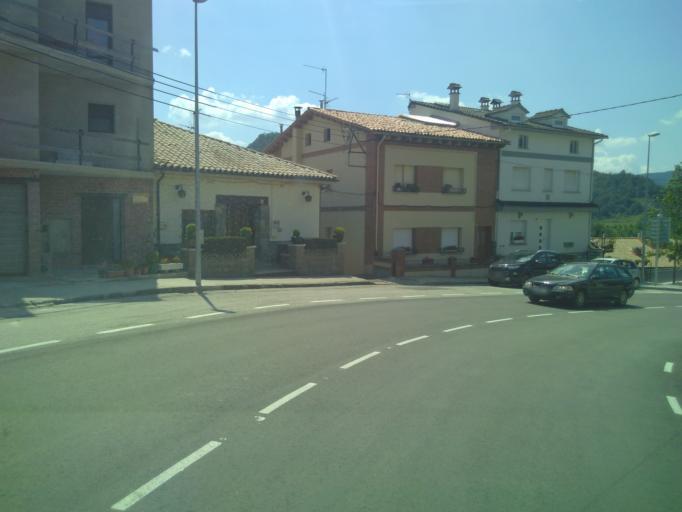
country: ES
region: Catalonia
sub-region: Provincia de Barcelona
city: Montesquiu
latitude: 42.1016
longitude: 2.2230
